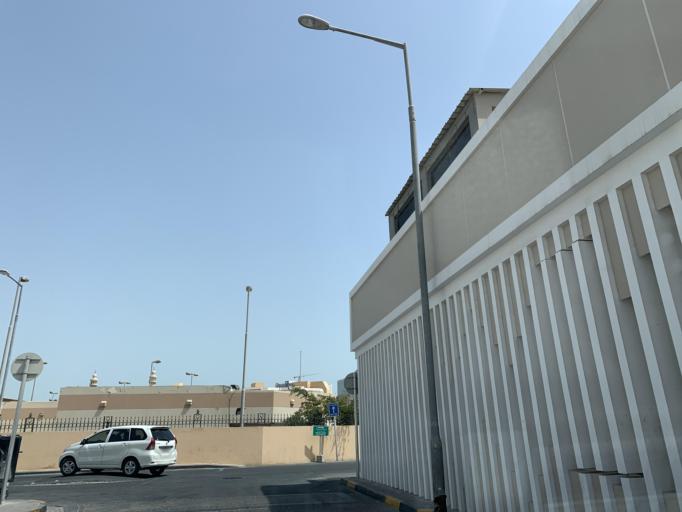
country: BH
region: Manama
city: Manama
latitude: 26.2140
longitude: 50.5948
